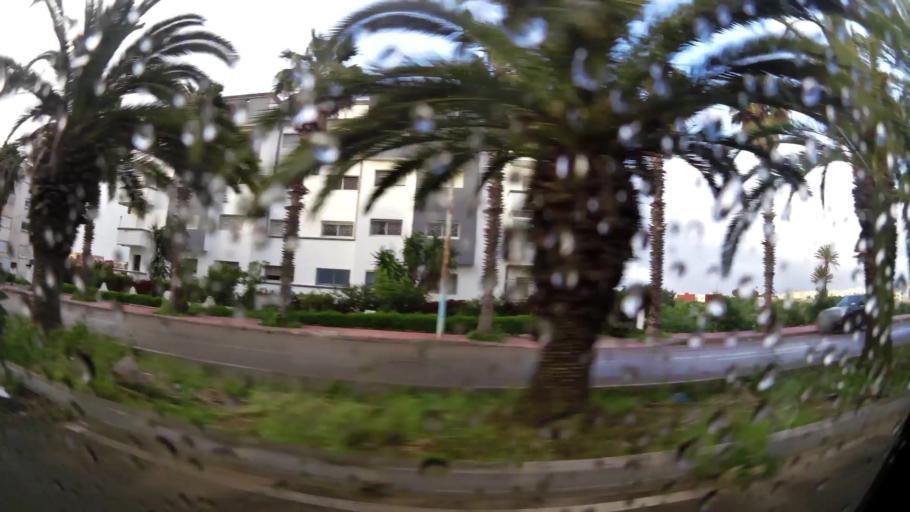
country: MA
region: Doukkala-Abda
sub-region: El-Jadida
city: El Jadida
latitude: 33.2316
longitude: -8.4904
